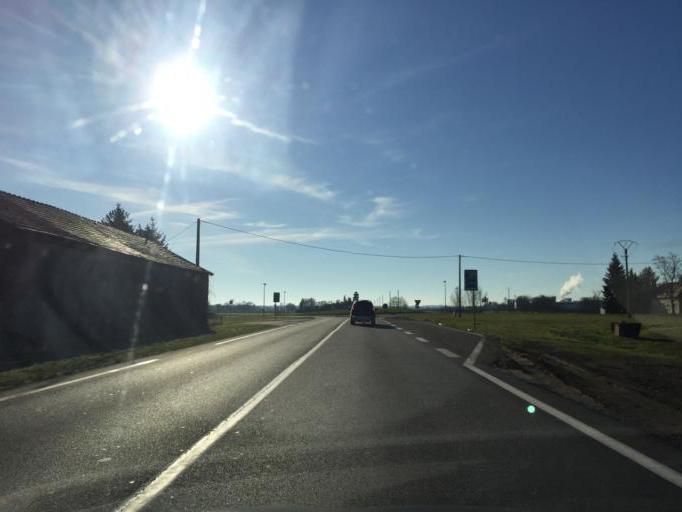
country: FR
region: Auvergne
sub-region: Departement de l'Allier
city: Saint-Pourcain-sur-Sioule
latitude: 46.2662
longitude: 3.2893
